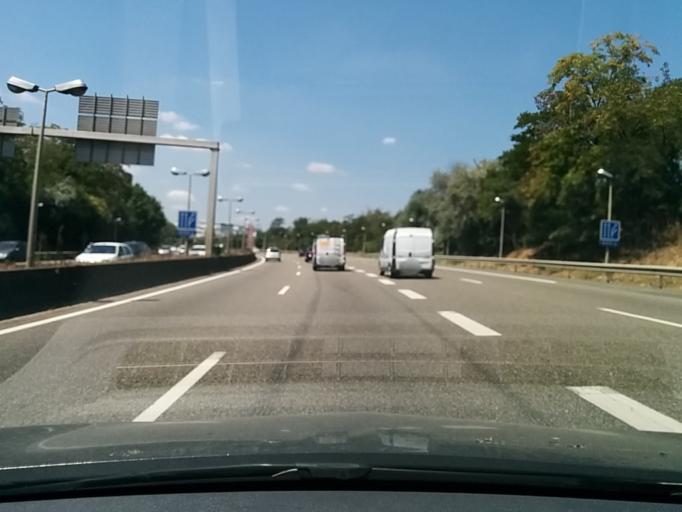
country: FR
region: Midi-Pyrenees
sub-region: Departement de la Haute-Garonne
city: Blagnac
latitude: 43.6112
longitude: 1.3829
